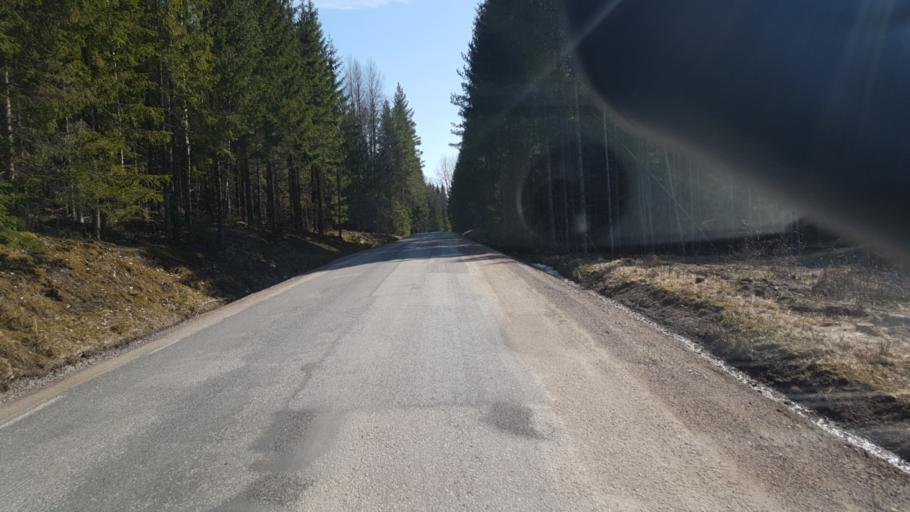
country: SE
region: Vaermland
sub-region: Arvika Kommun
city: Arvika
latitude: 59.6514
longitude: 12.8082
